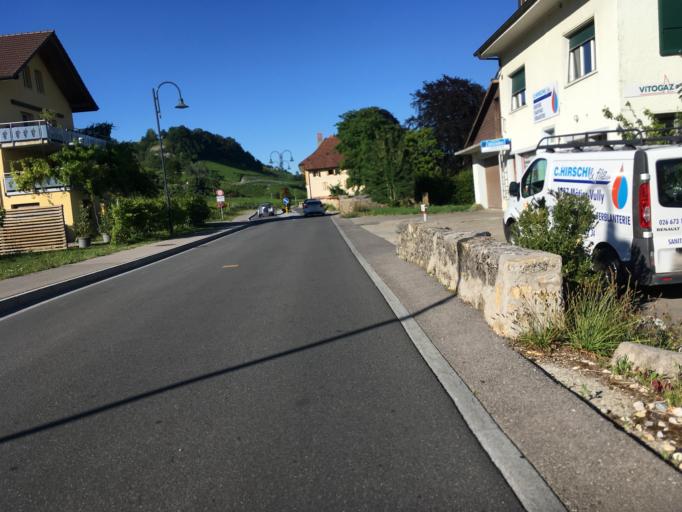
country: CH
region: Fribourg
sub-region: See District
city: Bas-Vully
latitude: 46.9512
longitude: 7.0915
